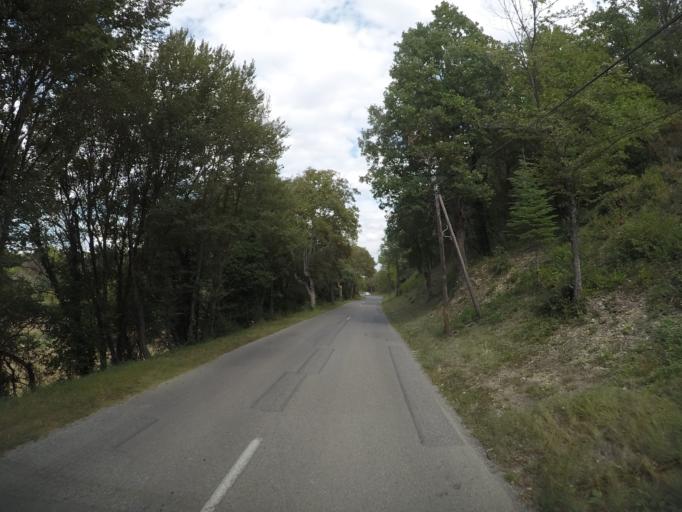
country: FR
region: Provence-Alpes-Cote d'Azur
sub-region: Departement des Alpes-de-Haute-Provence
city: Valensole
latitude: 43.8281
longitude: 5.9759
